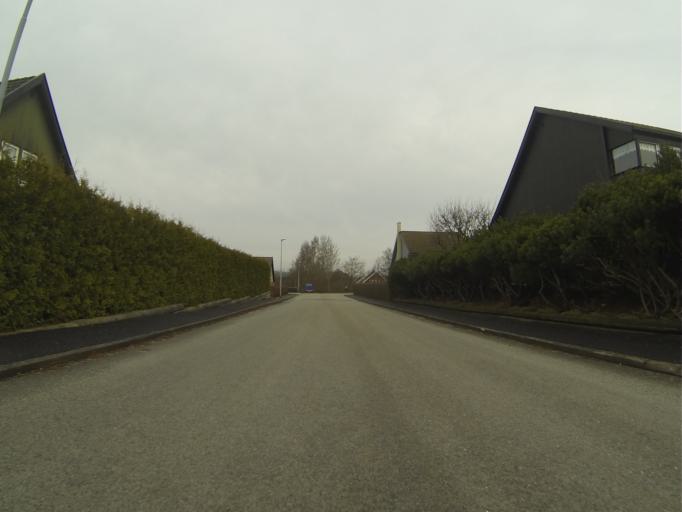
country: SE
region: Skane
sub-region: Lunds Kommun
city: Genarp
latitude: 55.7072
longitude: 13.3317
